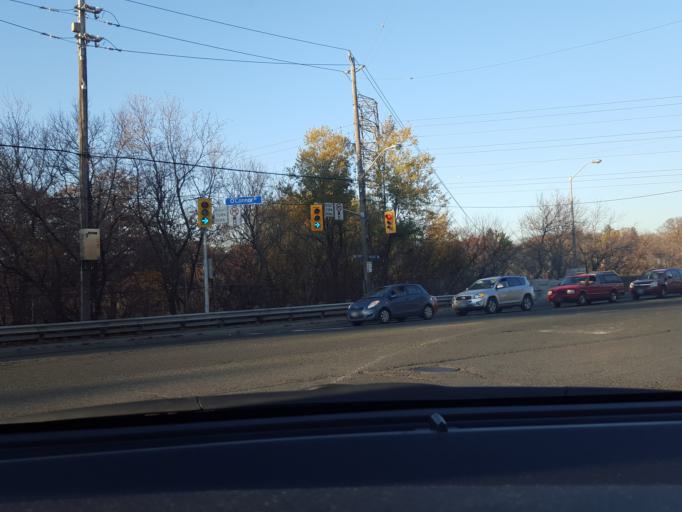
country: CA
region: Ontario
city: Scarborough
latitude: 43.7000
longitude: -79.3188
